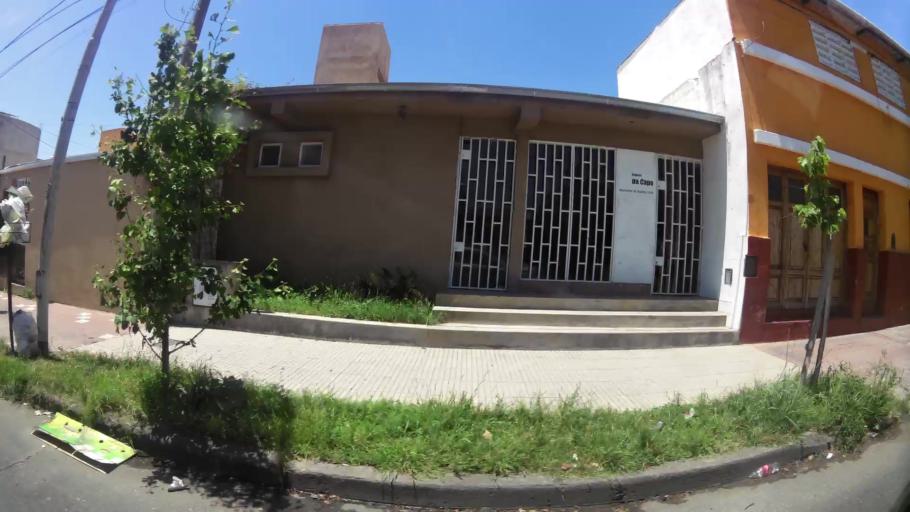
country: AR
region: Cordoba
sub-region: Departamento de Capital
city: Cordoba
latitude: -31.3932
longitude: -64.2127
